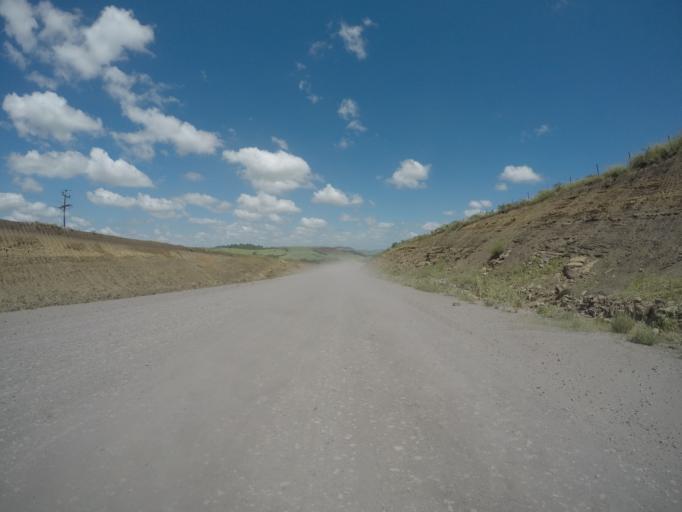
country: ZA
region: KwaZulu-Natal
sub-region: uThungulu District Municipality
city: Empangeni
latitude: -28.6354
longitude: 31.7627
